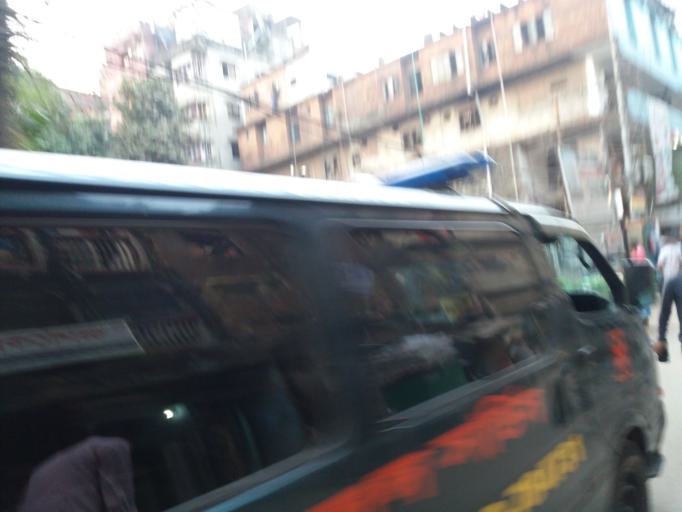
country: BD
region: Dhaka
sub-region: Dhaka
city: Dhaka
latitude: 23.7163
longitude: 90.4026
